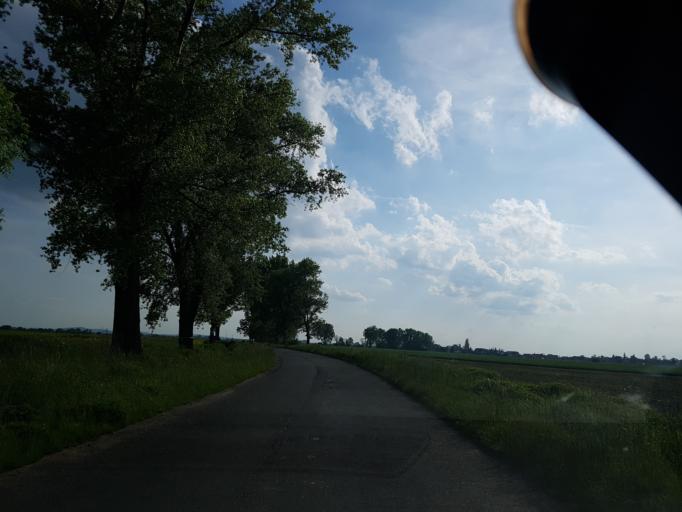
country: PL
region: Lower Silesian Voivodeship
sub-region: Powiat strzelinski
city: Wiazow
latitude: 50.8435
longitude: 17.2308
